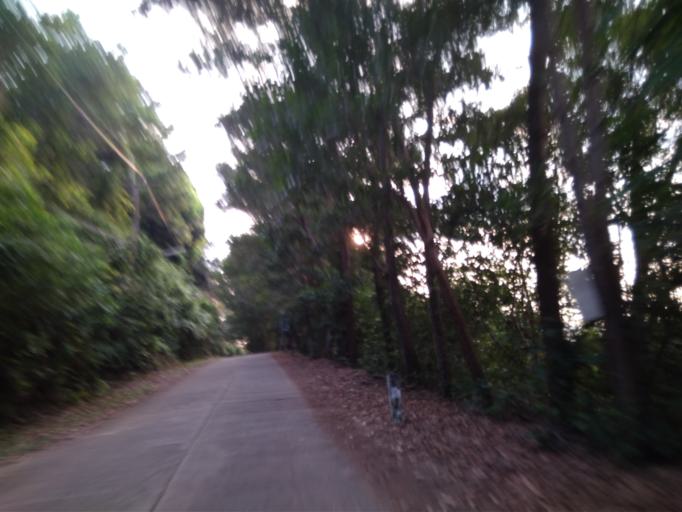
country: TH
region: Phangnga
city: Ko Yao
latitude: 8.1559
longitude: 98.6032
